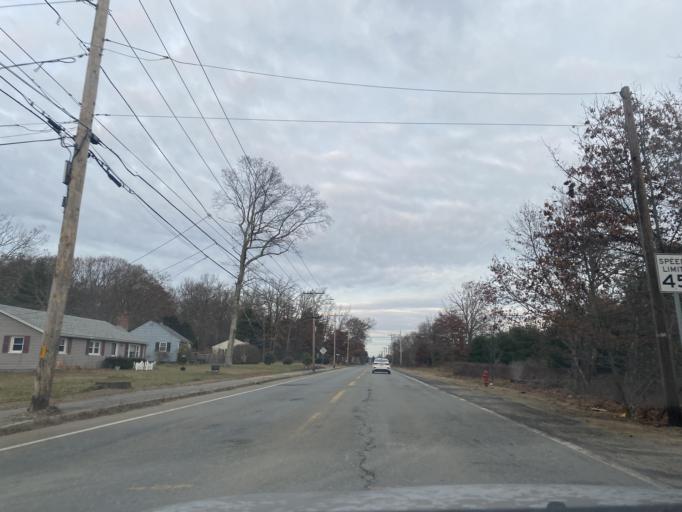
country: US
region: Massachusetts
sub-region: Worcester County
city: East Brookfield
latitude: 42.2202
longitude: -72.0694
